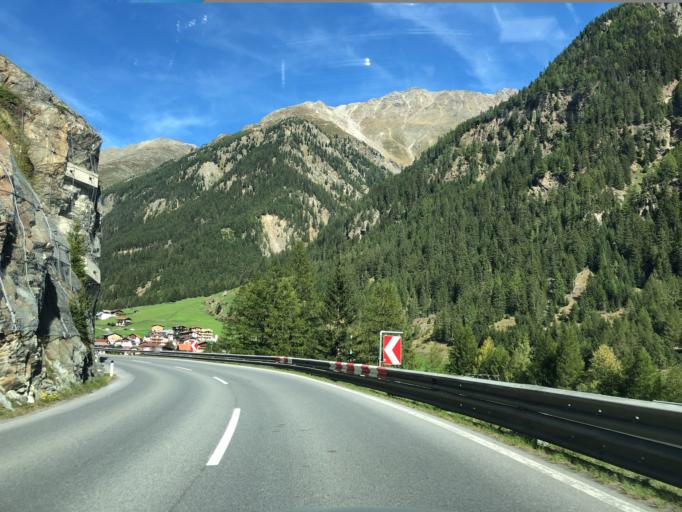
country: AT
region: Tyrol
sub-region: Politischer Bezirk Imst
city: Soelden
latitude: 46.9820
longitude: 11.0119
